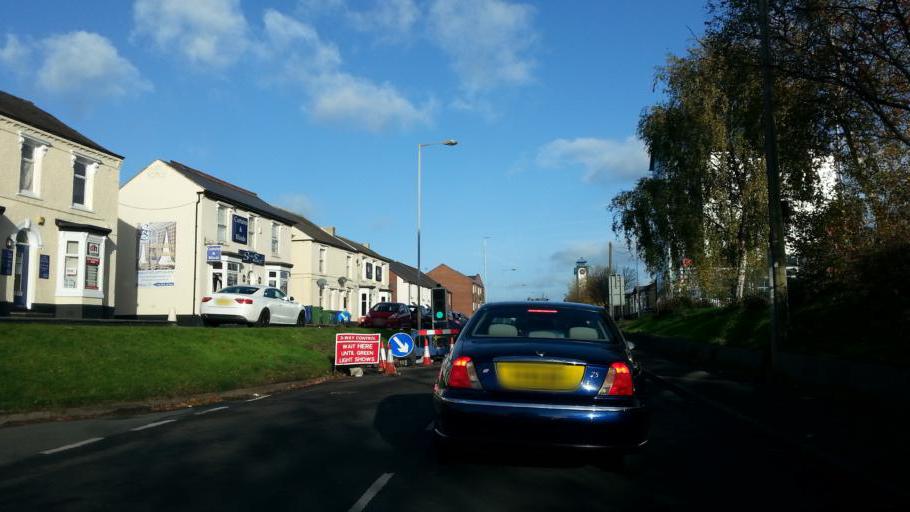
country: GB
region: England
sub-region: Staffordshire
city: Cannock
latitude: 52.6749
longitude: -2.0250
